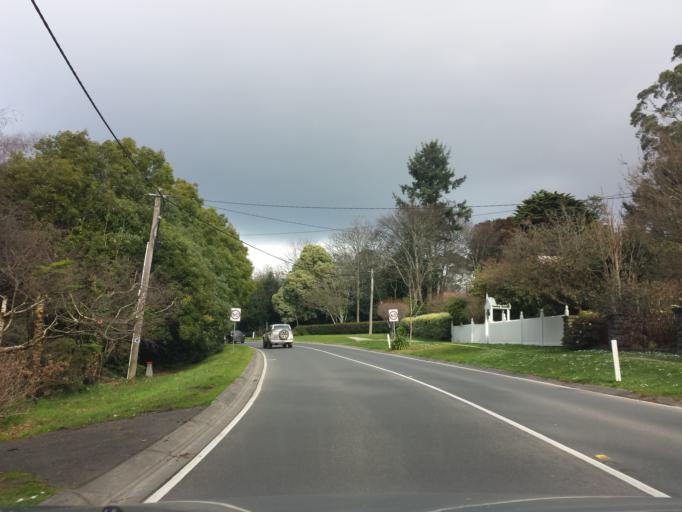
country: AU
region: Victoria
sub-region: Yarra Ranges
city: Ferny Creek
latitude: -37.8800
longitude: 145.3406
